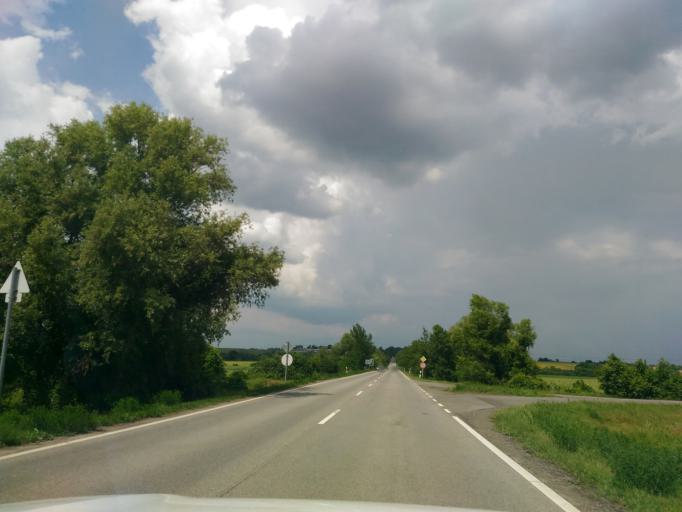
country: HU
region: Baranya
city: Hidas
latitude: 46.2649
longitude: 18.5114
